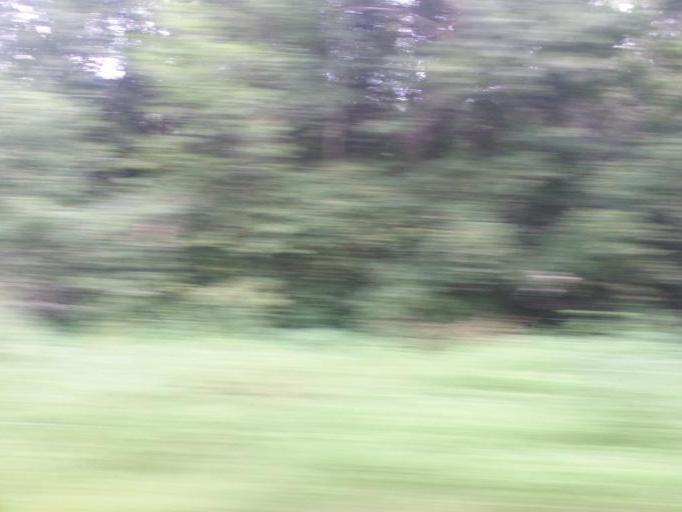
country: US
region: Tennessee
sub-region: Anderson County
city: Rocky Top
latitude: 36.1711
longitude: -84.1888
